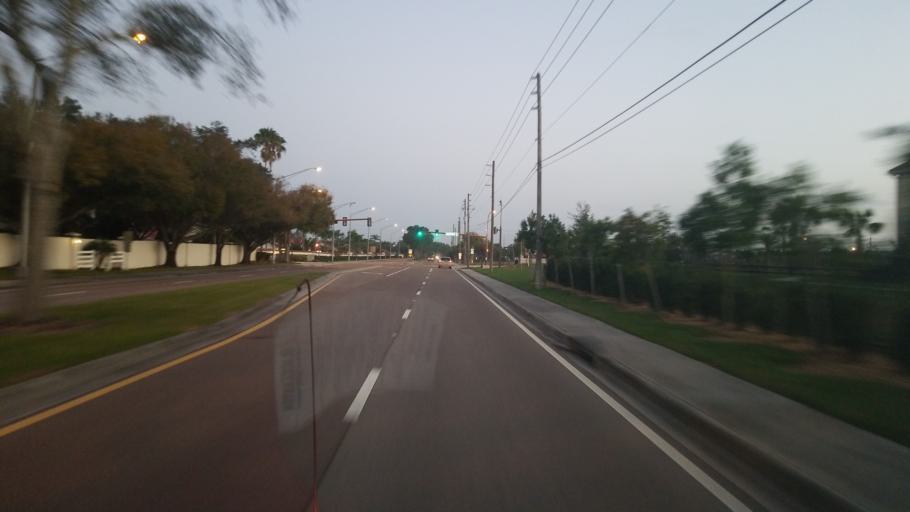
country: US
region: Florida
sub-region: Sarasota County
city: Lake Sarasota
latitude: 27.2878
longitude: -82.4521
